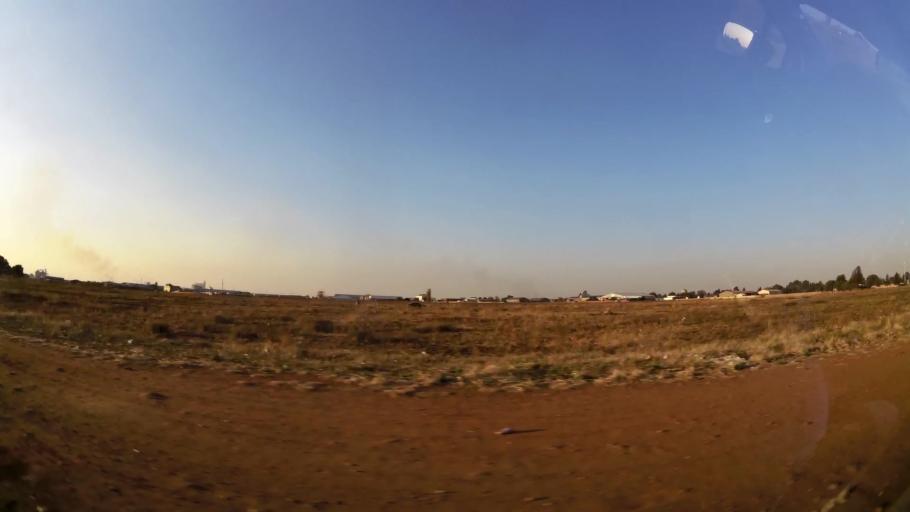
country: ZA
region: Gauteng
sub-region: West Rand District Municipality
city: Randfontein
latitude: -26.2059
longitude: 27.6901
